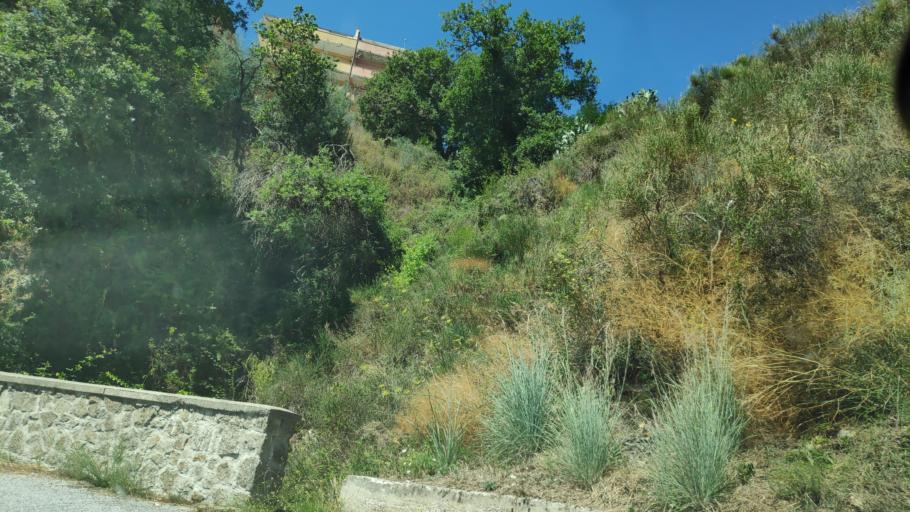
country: IT
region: Calabria
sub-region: Provincia di Catanzaro
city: Gasperina
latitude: 38.7425
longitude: 16.5076
